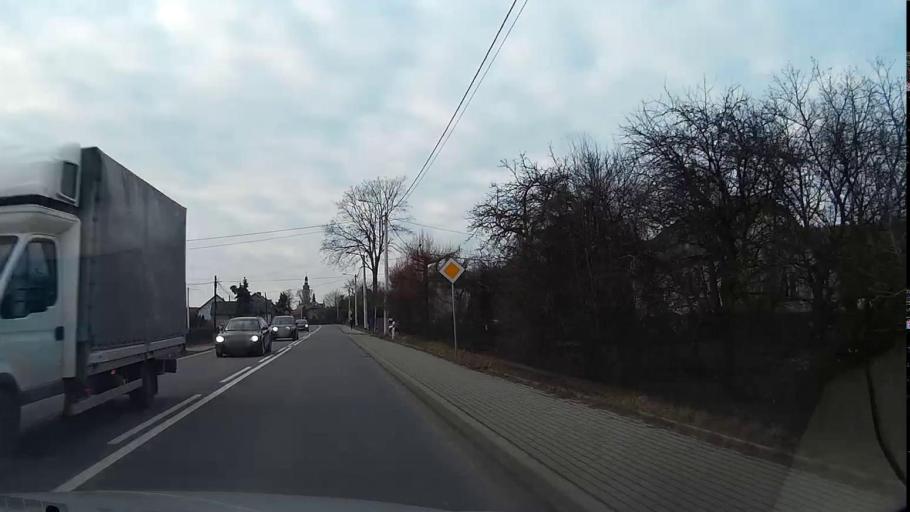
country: PL
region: Lesser Poland Voivodeship
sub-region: Powiat chrzanowski
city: Babice
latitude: 50.0701
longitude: 19.4589
